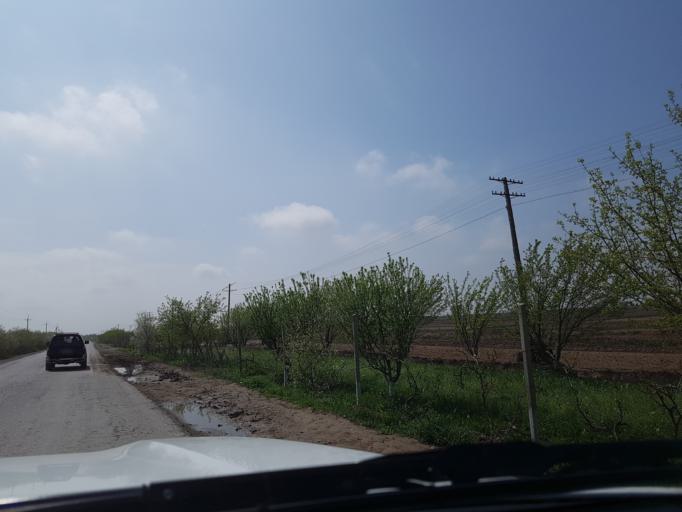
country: TM
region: Lebap
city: Turkmenabat
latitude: 38.9659
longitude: 63.6803
